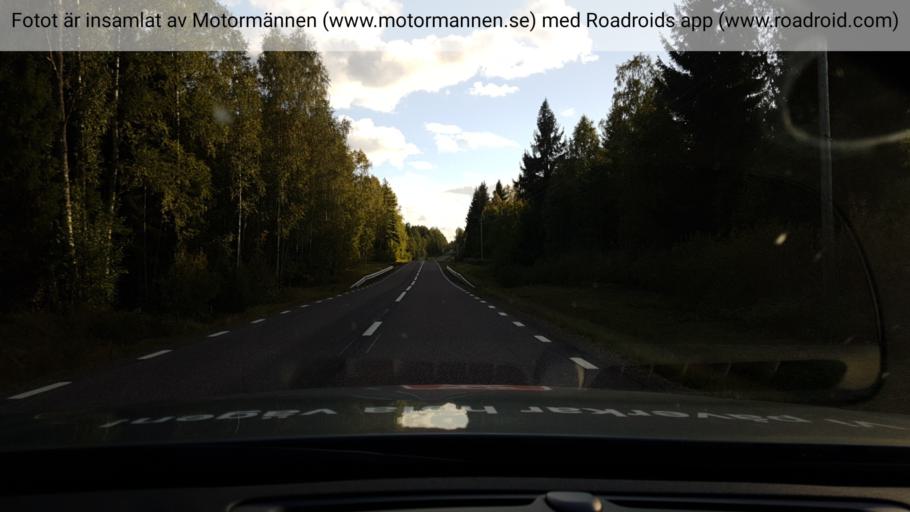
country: SE
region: Vaermland
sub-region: Karlstads Kommun
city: Molkom
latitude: 59.7582
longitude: 13.6935
